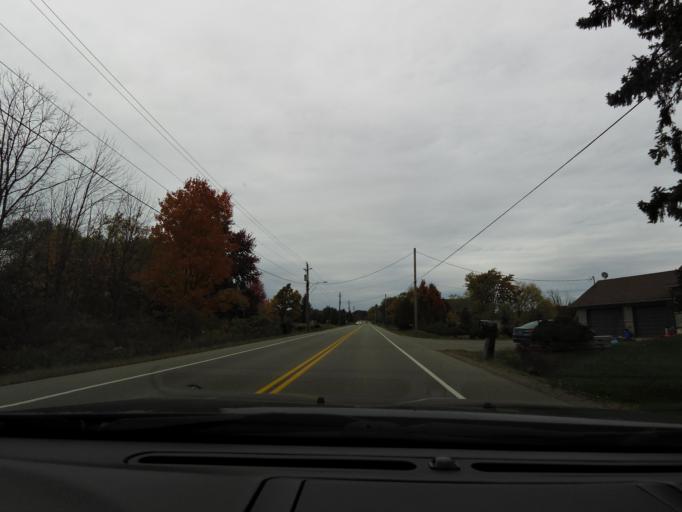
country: CA
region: Ontario
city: Hamilton
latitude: 43.3060
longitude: -79.8887
